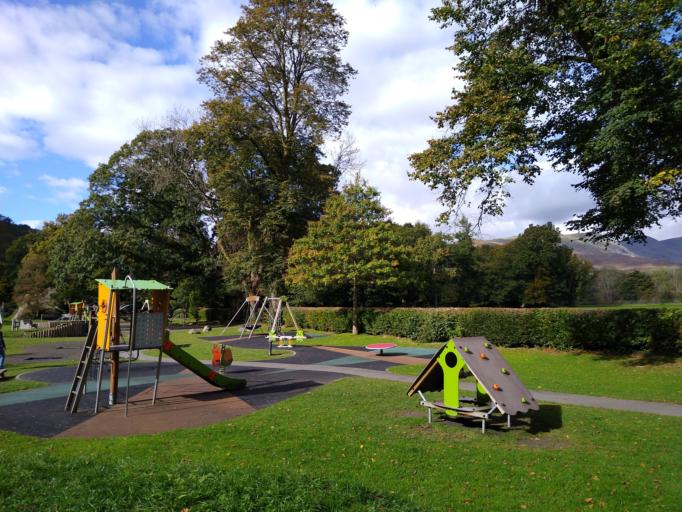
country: GB
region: England
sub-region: Cumbria
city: Ambleside
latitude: 54.4311
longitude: -2.9675
